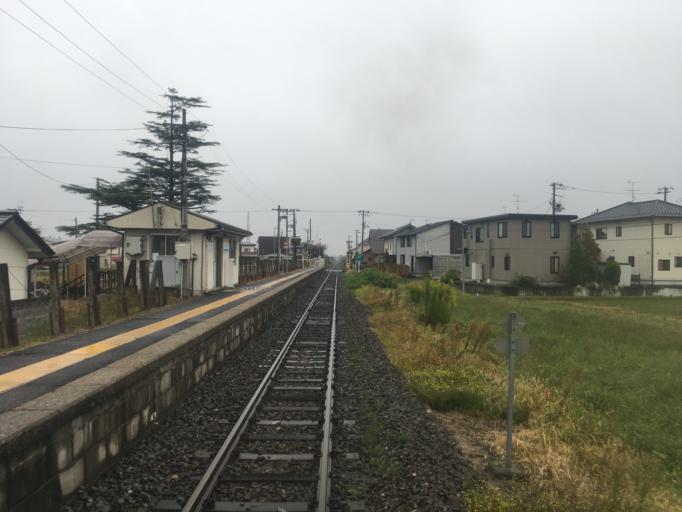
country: JP
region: Miyagi
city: Furukawa
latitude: 38.5725
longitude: 140.9368
